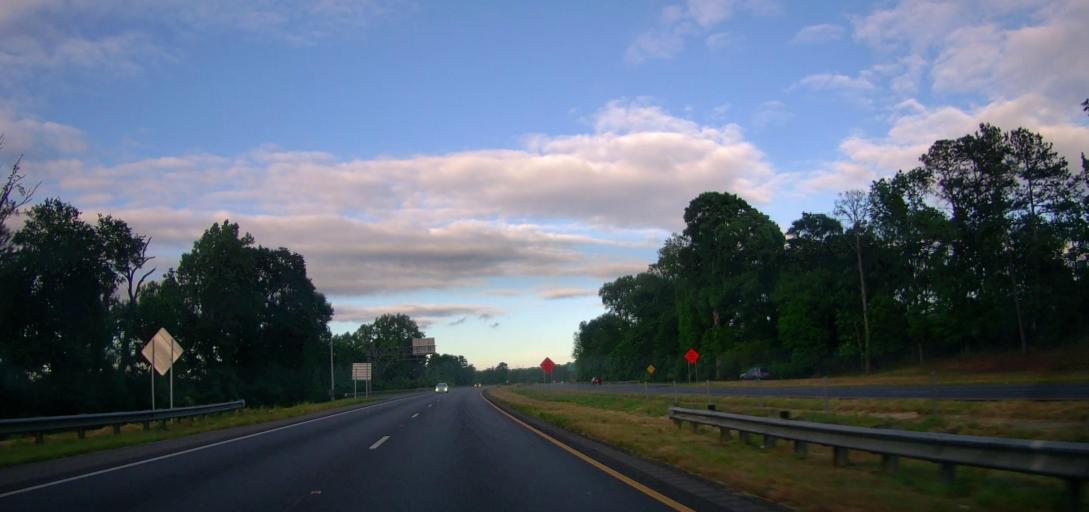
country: US
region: Georgia
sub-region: Clarke County
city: Athens
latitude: 33.9744
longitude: -83.3920
